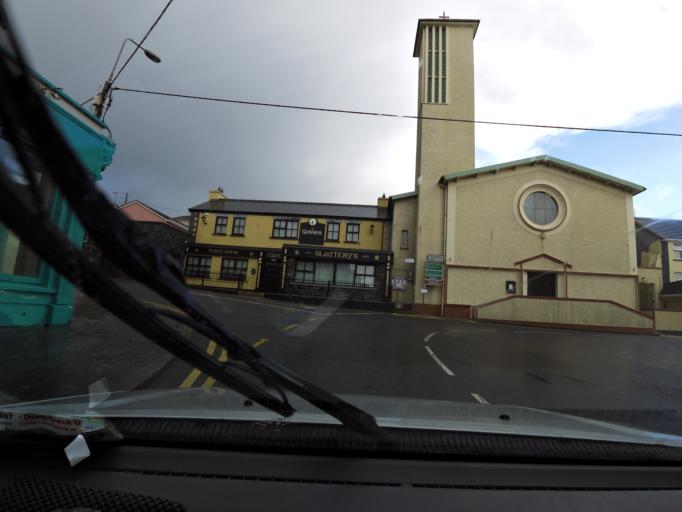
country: IE
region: Munster
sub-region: An Clar
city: Kilrush
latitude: 52.9315
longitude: -9.3456
